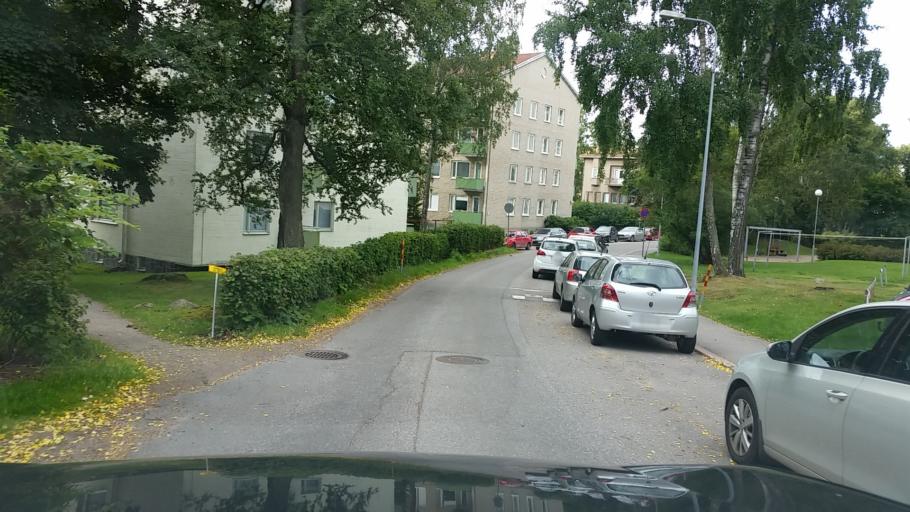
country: FI
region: Uusimaa
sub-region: Helsinki
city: Helsinki
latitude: 60.1601
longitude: 24.8848
